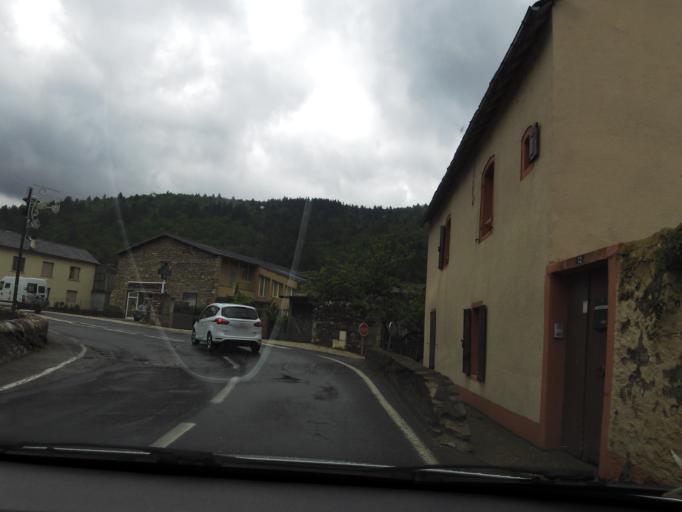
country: FR
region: Languedoc-Roussillon
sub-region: Departement de la Lozere
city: Florac
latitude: 44.3703
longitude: 3.5374
